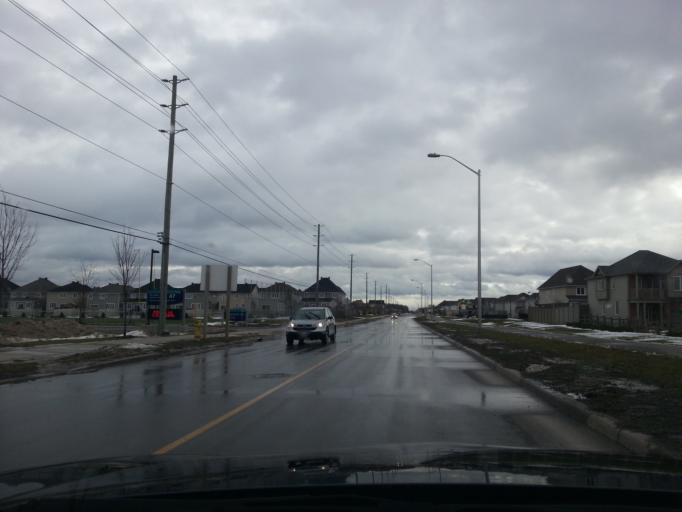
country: CA
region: Ontario
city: Bells Corners
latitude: 45.2521
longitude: -75.7353
